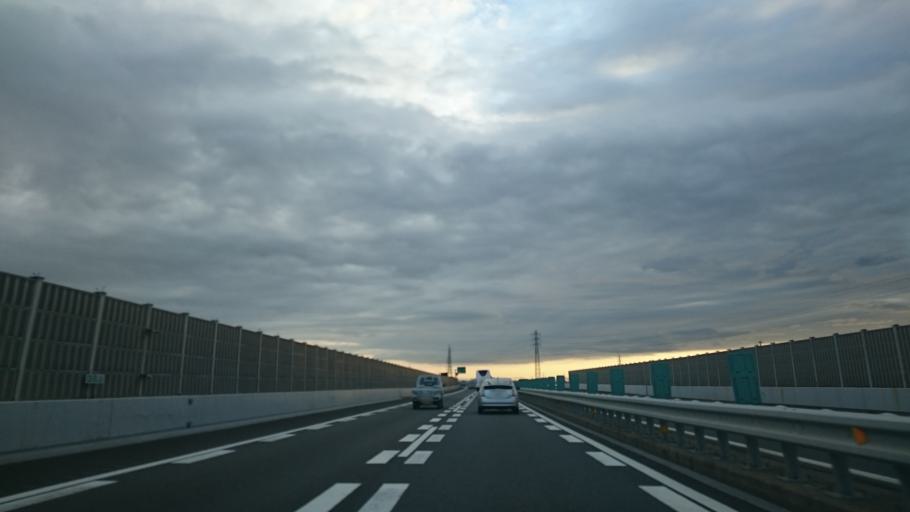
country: JP
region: Aichi
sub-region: Aisai-shi
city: Aisai
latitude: 35.1239
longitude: 136.7201
